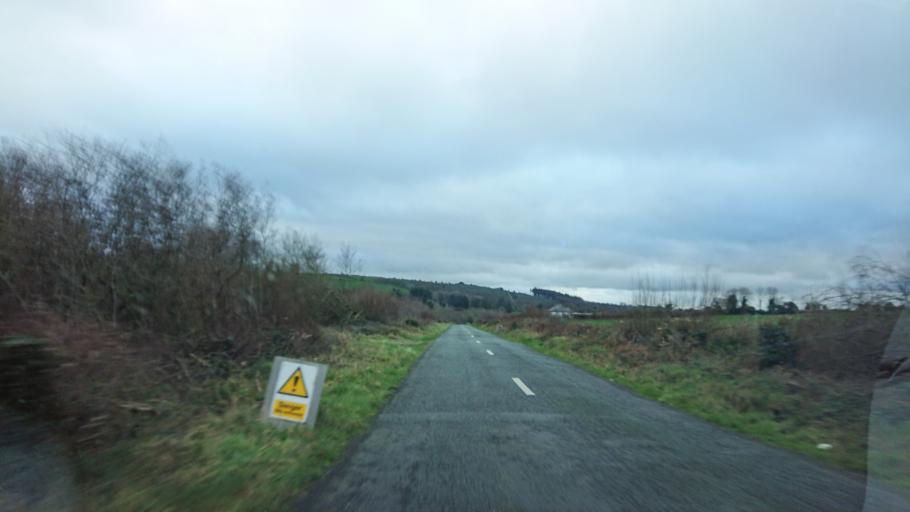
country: IE
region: Munster
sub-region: Waterford
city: Portlaw
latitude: 52.2317
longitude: -7.4106
